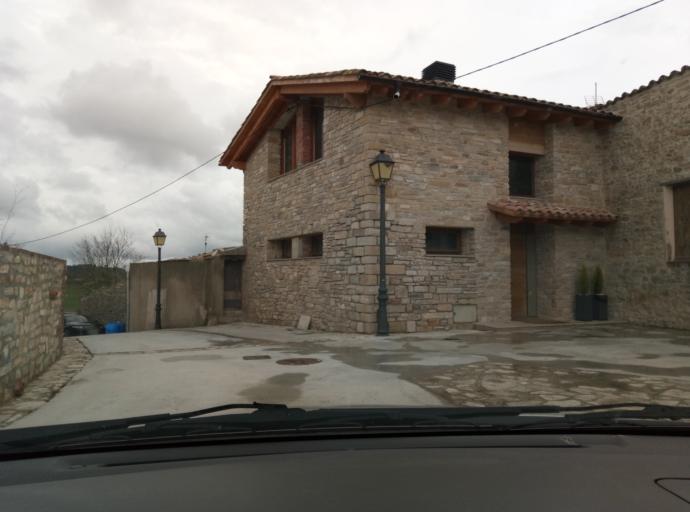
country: ES
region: Catalonia
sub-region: Provincia de Tarragona
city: Santa Coloma de Queralt
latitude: 41.5426
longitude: 1.3595
